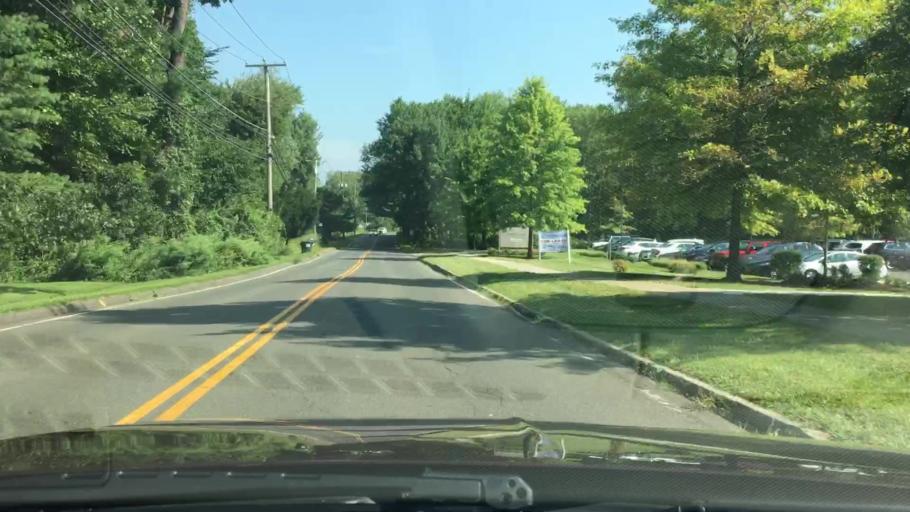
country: US
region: Connecticut
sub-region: Fairfield County
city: Danbury
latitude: 41.3710
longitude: -73.4919
